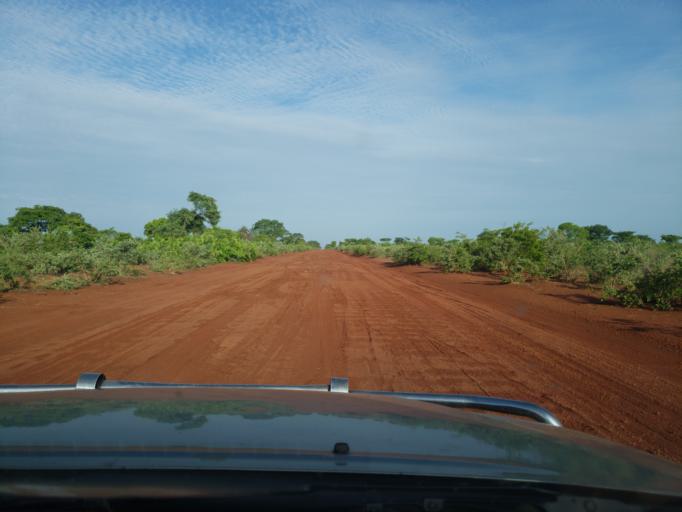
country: ML
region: Sikasso
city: Koutiala
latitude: 12.4282
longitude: -5.6261
